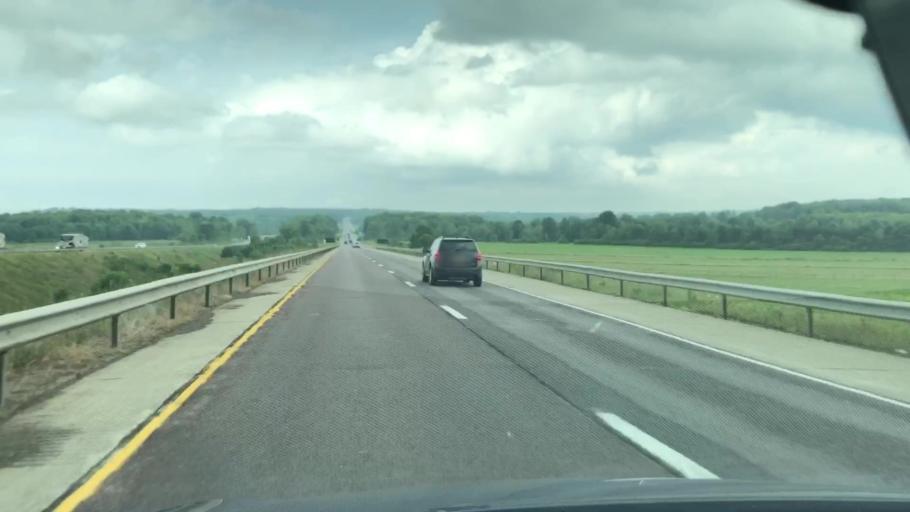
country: US
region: Pennsylvania
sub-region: Erie County
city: Fairview
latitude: 41.9862
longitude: -80.1737
